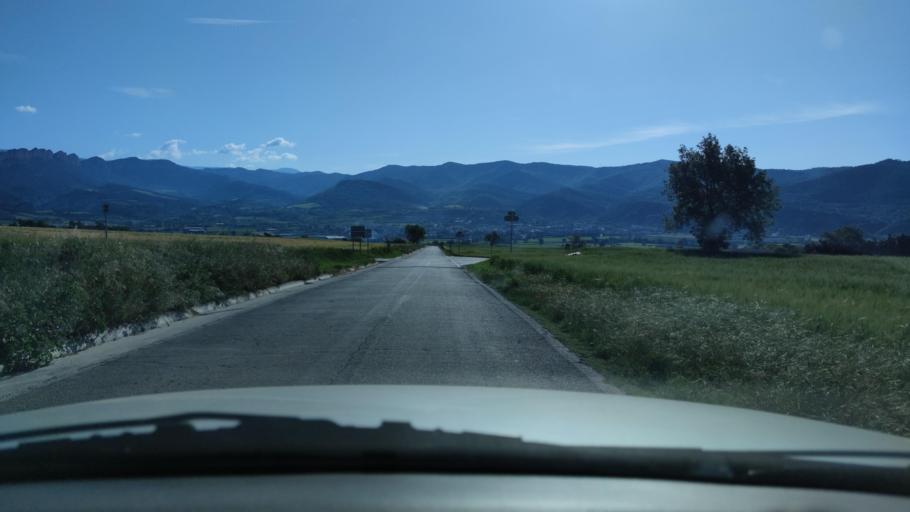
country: ES
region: Catalonia
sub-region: Provincia de Lleida
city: Oliana
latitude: 42.0653
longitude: 1.2882
